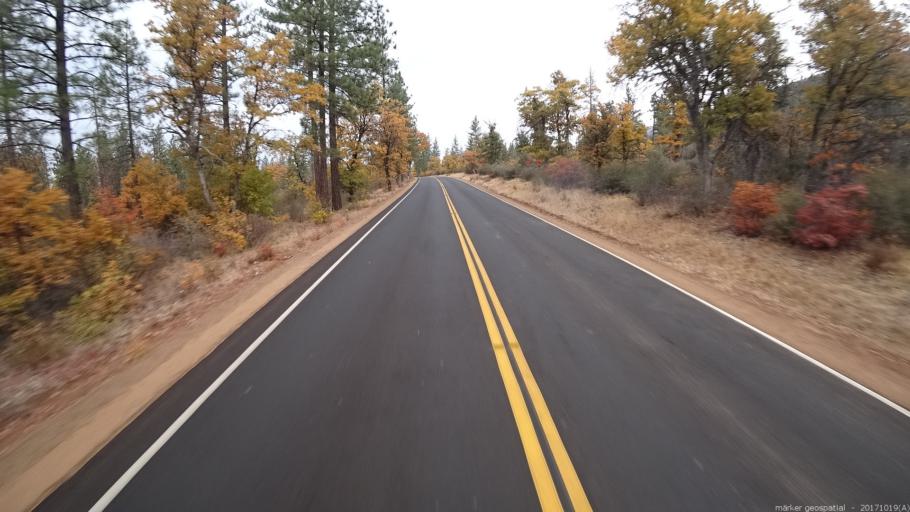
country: US
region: California
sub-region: Shasta County
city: Burney
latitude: 41.1572
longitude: -121.3551
